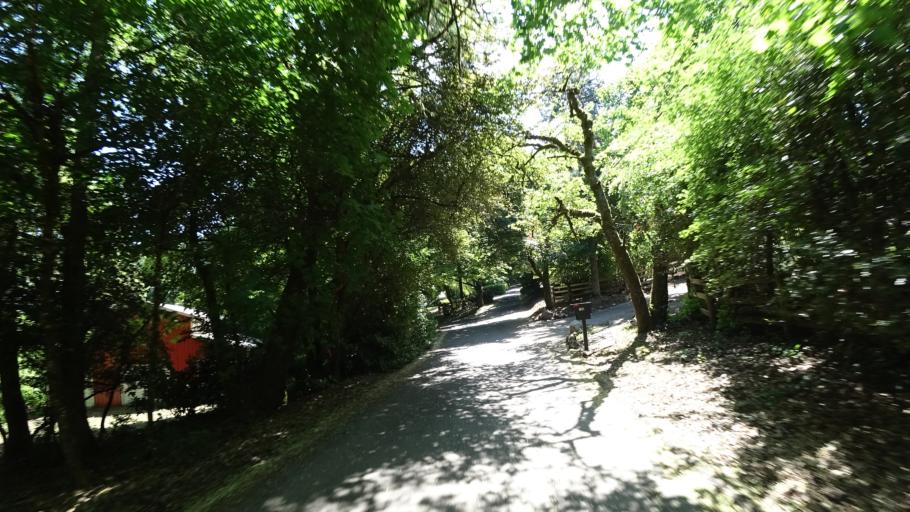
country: US
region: Oregon
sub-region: Clackamas County
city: Lake Oswego
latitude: 45.4349
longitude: -122.6948
